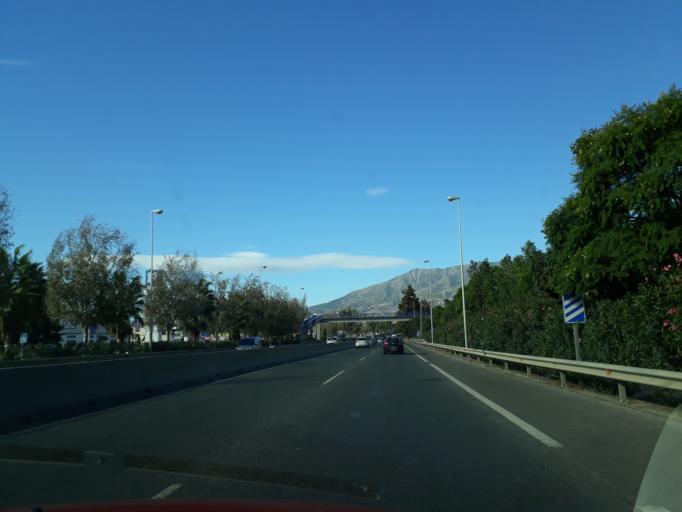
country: ES
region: Andalusia
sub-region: Provincia de Malaga
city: Fuengirola
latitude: 36.5350
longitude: -4.6330
